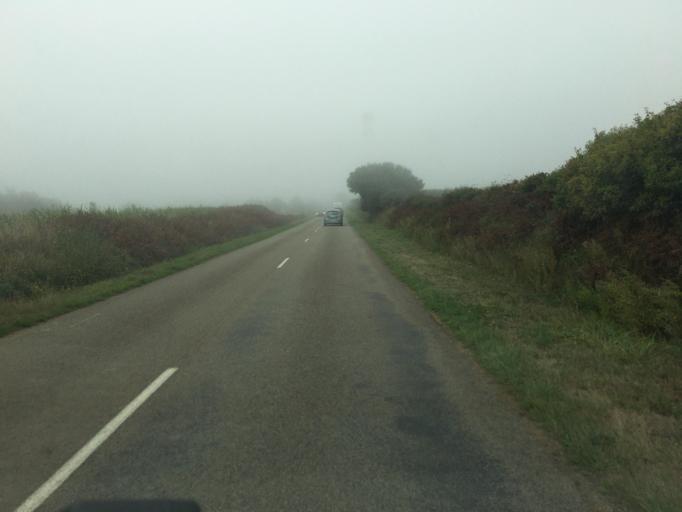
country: FR
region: Brittany
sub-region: Departement du Finistere
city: Plogoff
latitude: 48.0568
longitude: -4.6906
